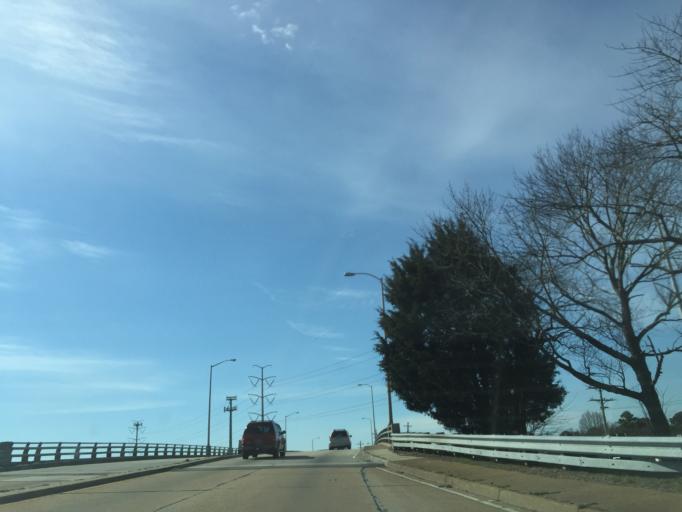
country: US
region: Virginia
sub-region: City of Norfolk
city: Norfolk
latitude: 36.8982
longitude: -76.2559
